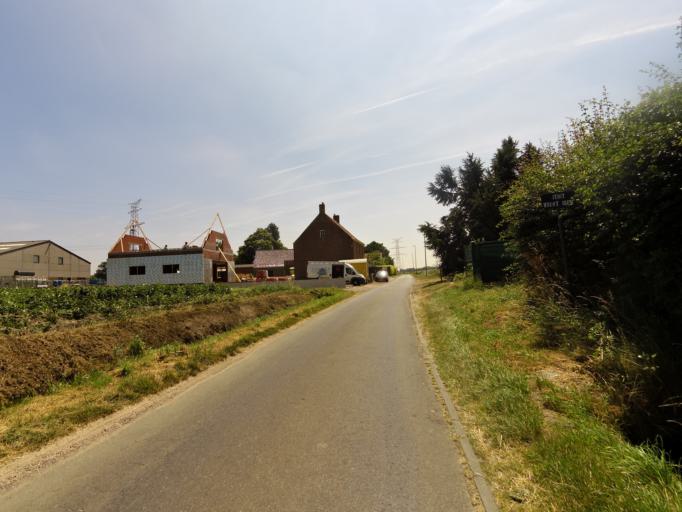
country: BE
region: Flanders
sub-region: Provincie West-Vlaanderen
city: Zedelgem
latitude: 51.1652
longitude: 3.1272
